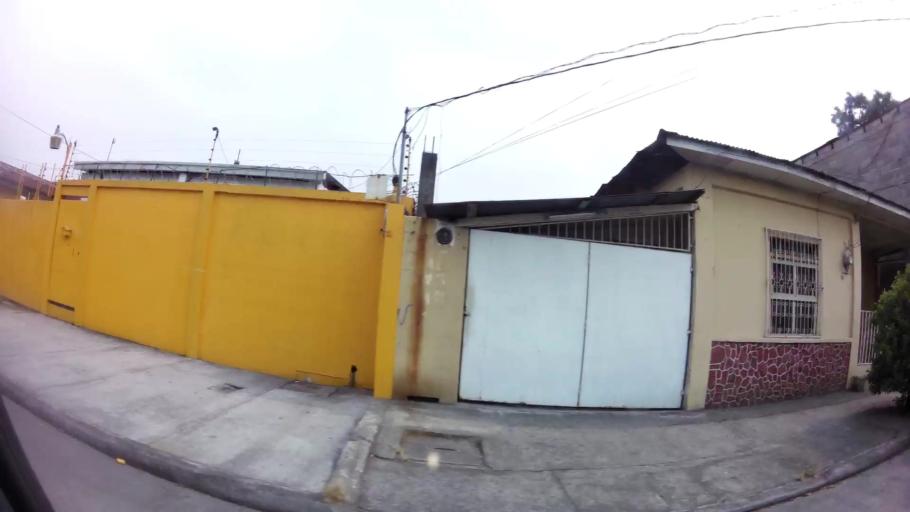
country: HN
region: Cortes
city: San Pedro Sula
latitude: 15.4952
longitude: -88.0301
